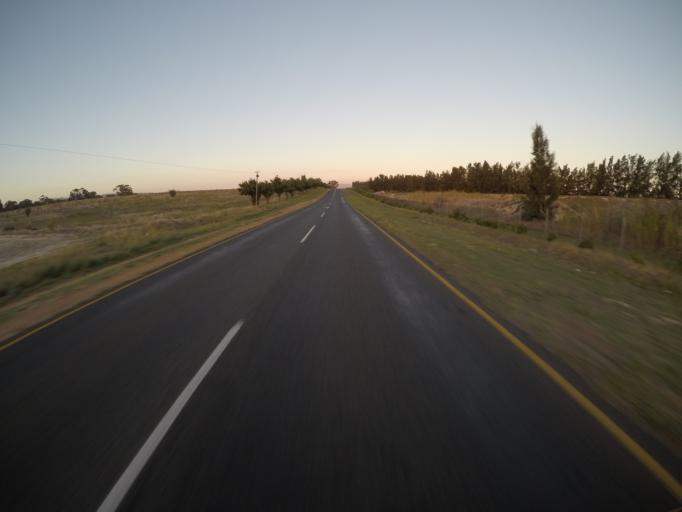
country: ZA
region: Western Cape
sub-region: Cape Winelands District Municipality
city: Paarl
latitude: -33.8055
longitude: 18.8818
